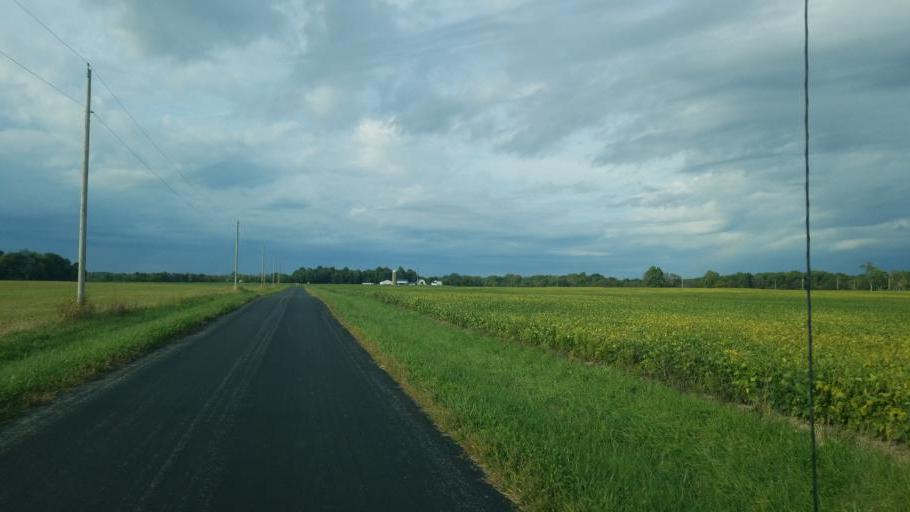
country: US
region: Ohio
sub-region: Wyandot County
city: Upper Sandusky
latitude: 40.9319
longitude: -83.1505
